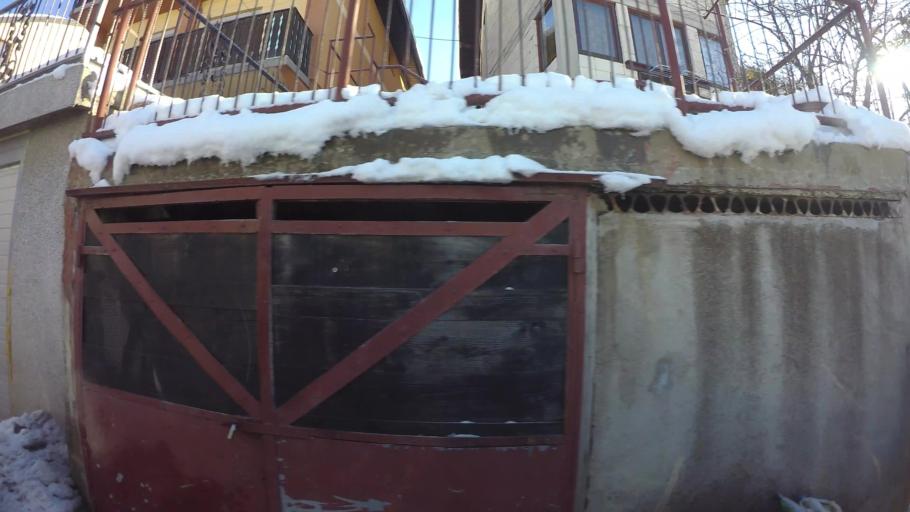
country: BA
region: Federation of Bosnia and Herzegovina
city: Kobilja Glava
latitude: 43.8758
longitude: 18.4224
